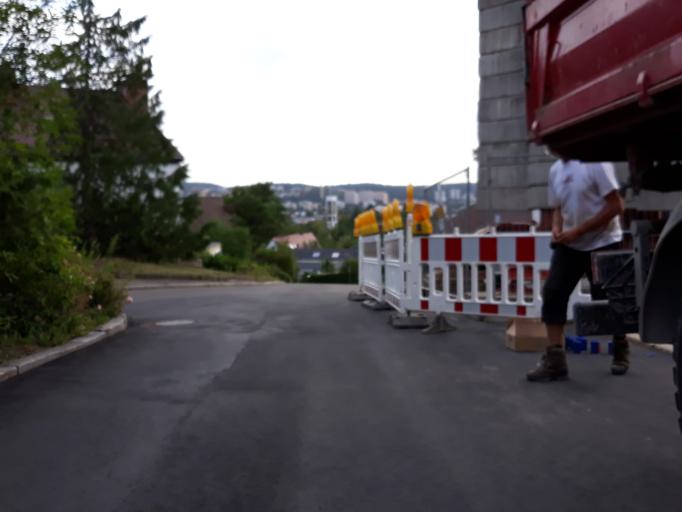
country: DE
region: Baden-Wuerttemberg
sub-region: Regierungsbezirk Stuttgart
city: Boeblingen
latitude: 48.6868
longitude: 9.0288
